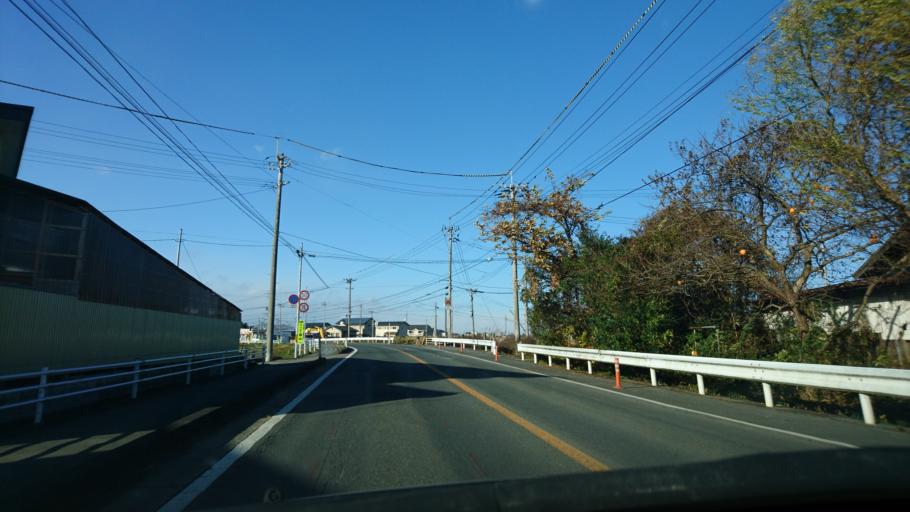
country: JP
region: Iwate
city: Mizusawa
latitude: 39.1247
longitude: 141.1632
